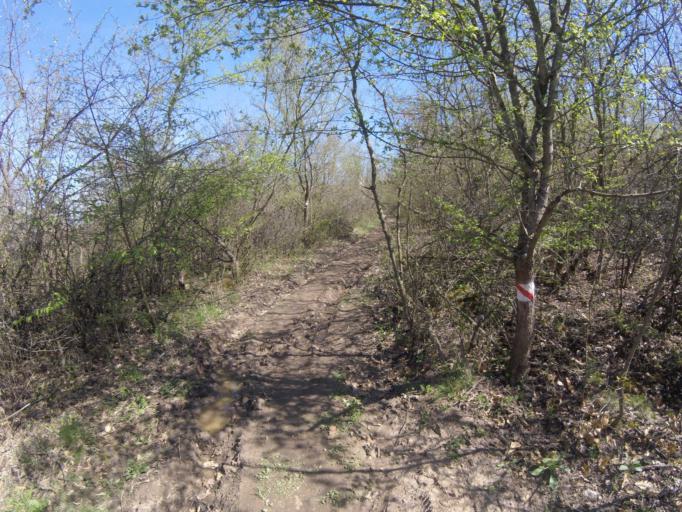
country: HU
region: Borsod-Abauj-Zemplen
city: Szendro
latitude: 48.4065
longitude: 20.7577
